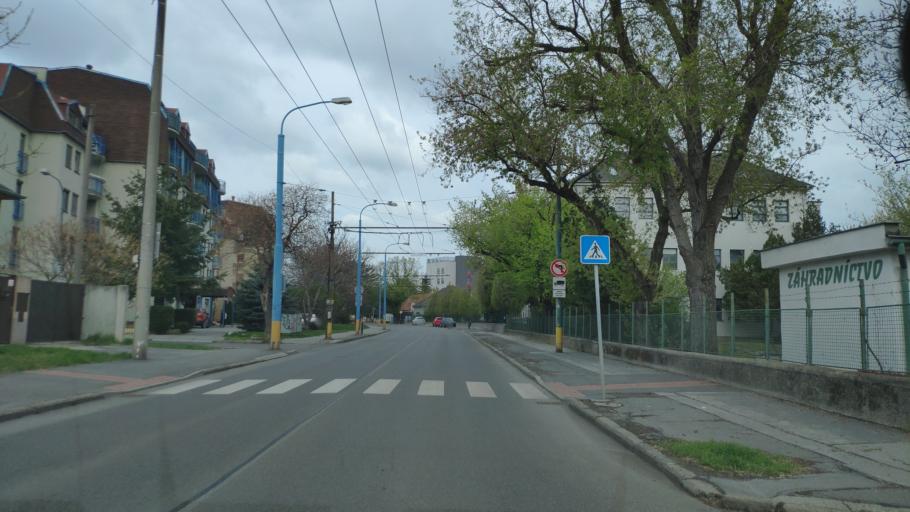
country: SK
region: Bratislavsky
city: Bratislava
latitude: 48.1493
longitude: 17.1753
